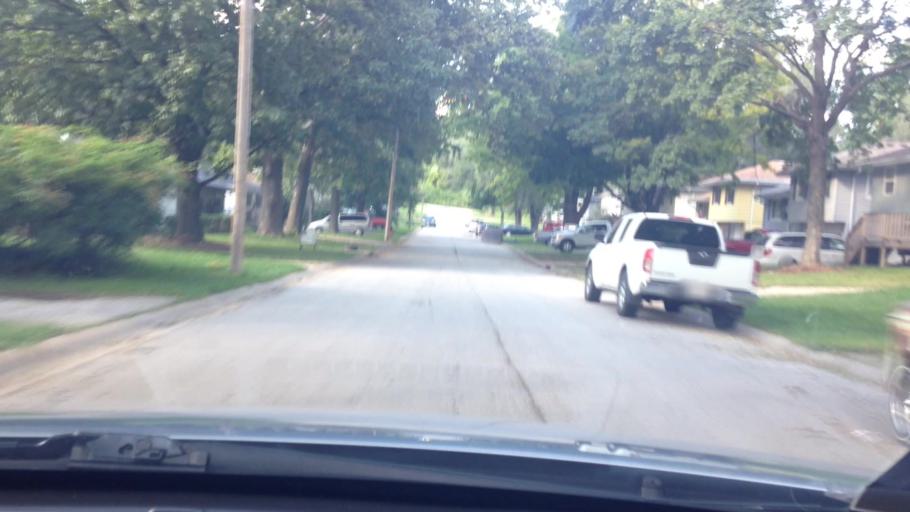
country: US
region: Missouri
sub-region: Clay County
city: Claycomo
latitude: 39.1788
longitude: -94.4978
